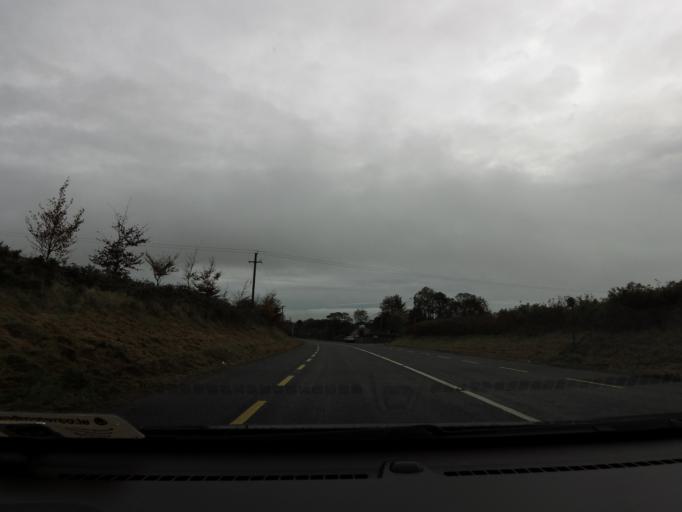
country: IE
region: Connaught
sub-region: County Galway
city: Tuam
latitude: 53.5677
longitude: -8.7901
